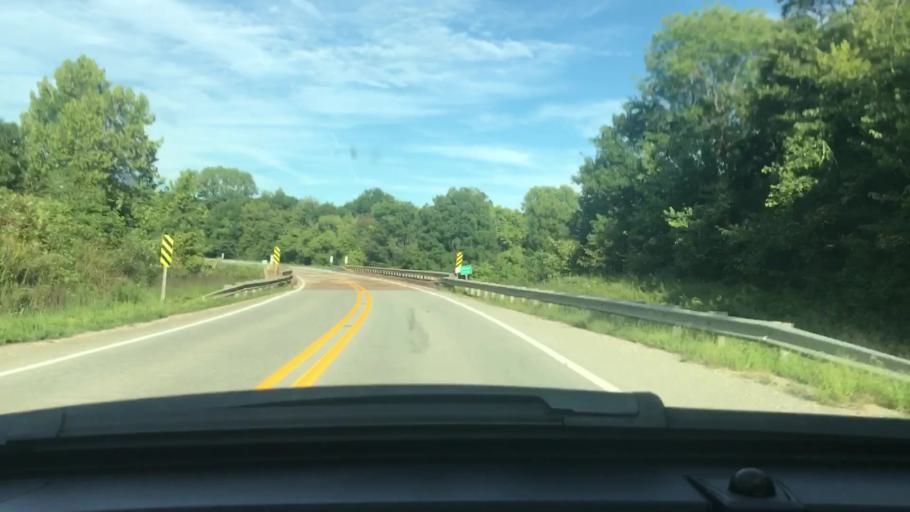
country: US
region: Arkansas
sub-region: Sharp County
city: Cherokee Village
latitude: 36.2730
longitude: -91.3336
